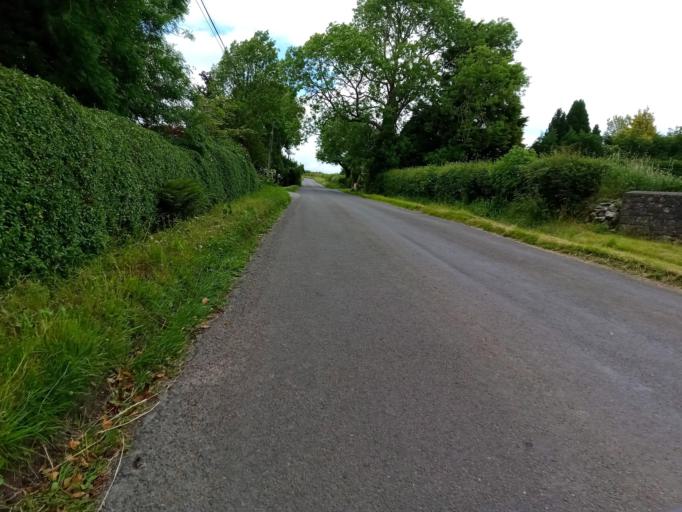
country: IE
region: Leinster
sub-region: Kilkenny
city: Kilkenny
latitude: 52.6929
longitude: -7.2486
